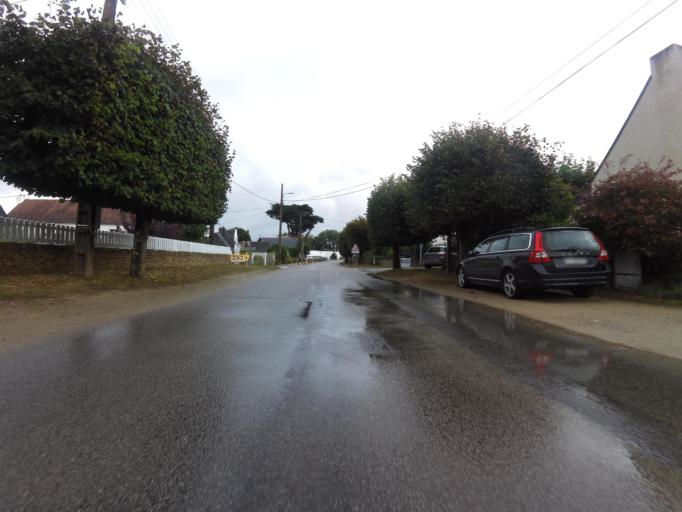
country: FR
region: Brittany
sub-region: Departement du Morbihan
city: Etel
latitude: 47.6617
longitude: -3.2035
